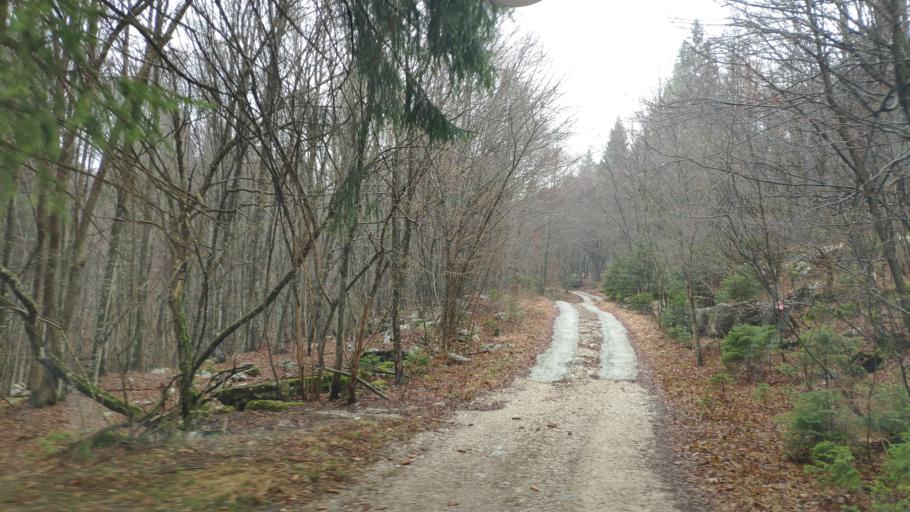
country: IT
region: Veneto
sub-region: Provincia di Vicenza
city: Rotzo
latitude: 45.8249
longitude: 11.3996
